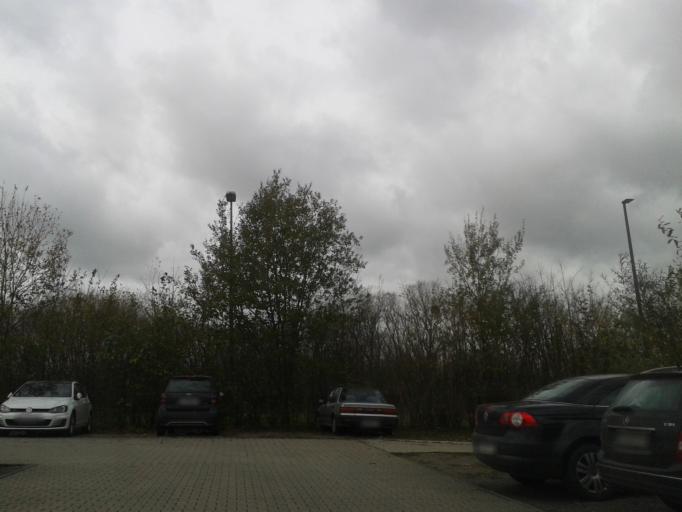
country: DE
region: North Rhine-Westphalia
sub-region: Regierungsbezirk Detmold
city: Lemgo
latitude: 52.0185
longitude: 8.9046
